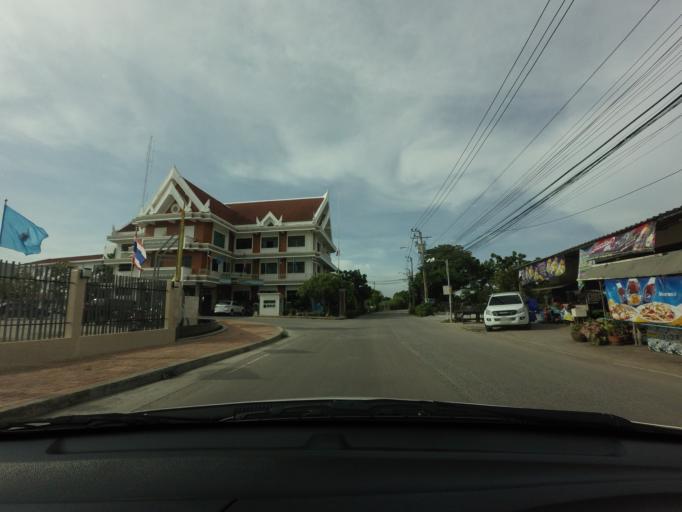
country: TH
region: Bangkok
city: Bang Na
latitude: 13.6367
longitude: 100.6642
